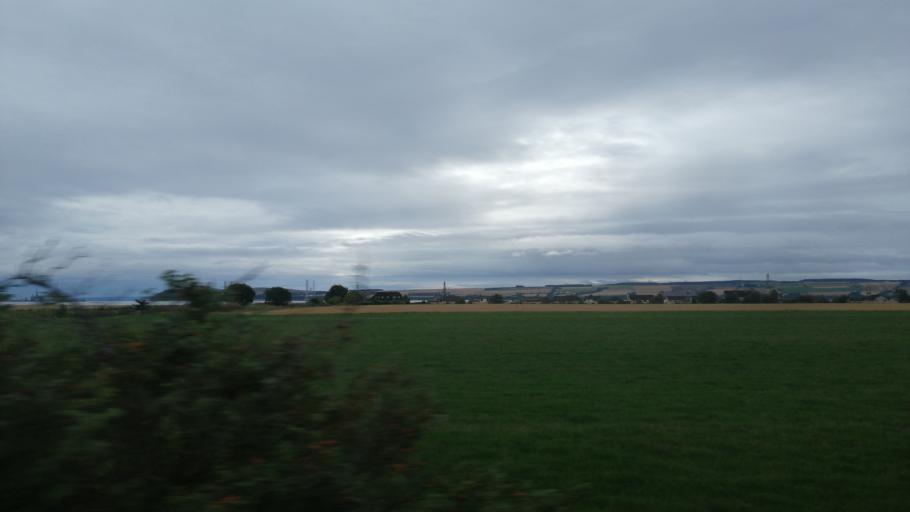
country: GB
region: Scotland
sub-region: Highland
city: Invergordon
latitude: 57.7064
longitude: -4.1406
